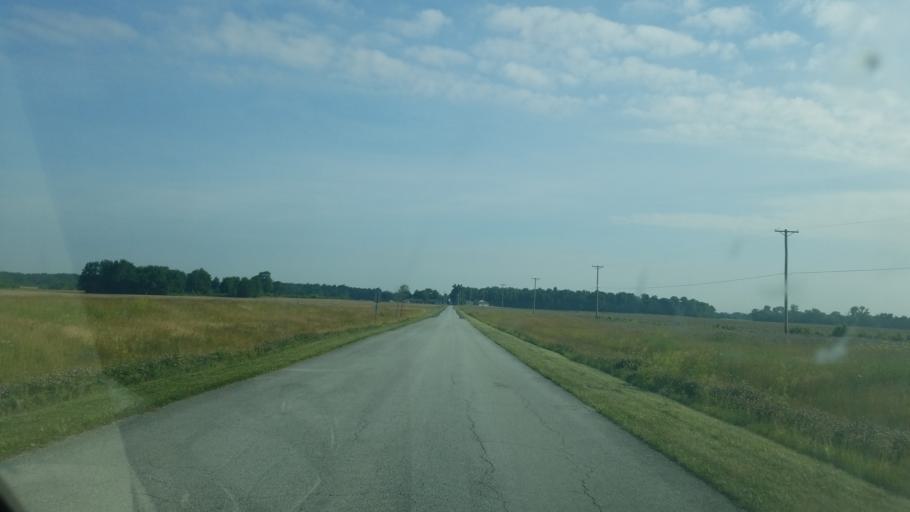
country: US
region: Ohio
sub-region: Hancock County
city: Arlington
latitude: 40.8278
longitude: -83.6705
